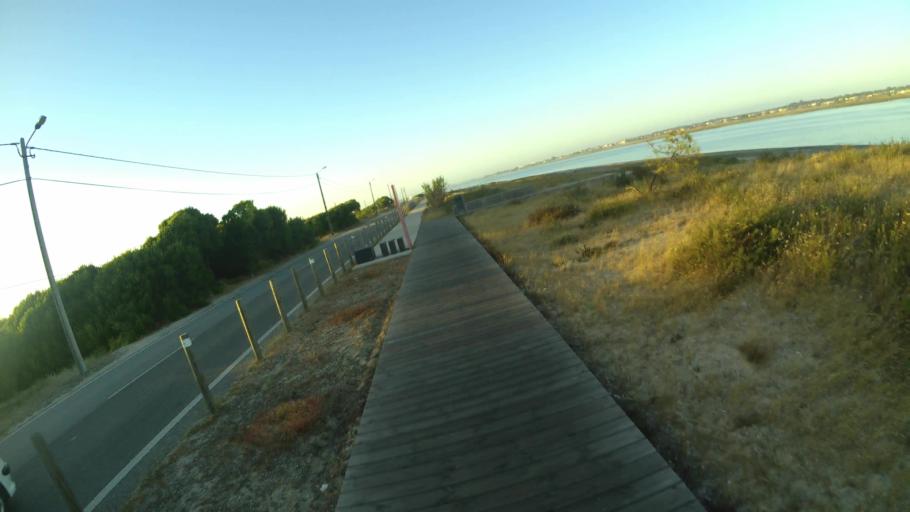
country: PT
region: Aveiro
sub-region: Ilhavo
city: Gafanha da Encarnacao
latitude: 40.6001
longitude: -8.7495
